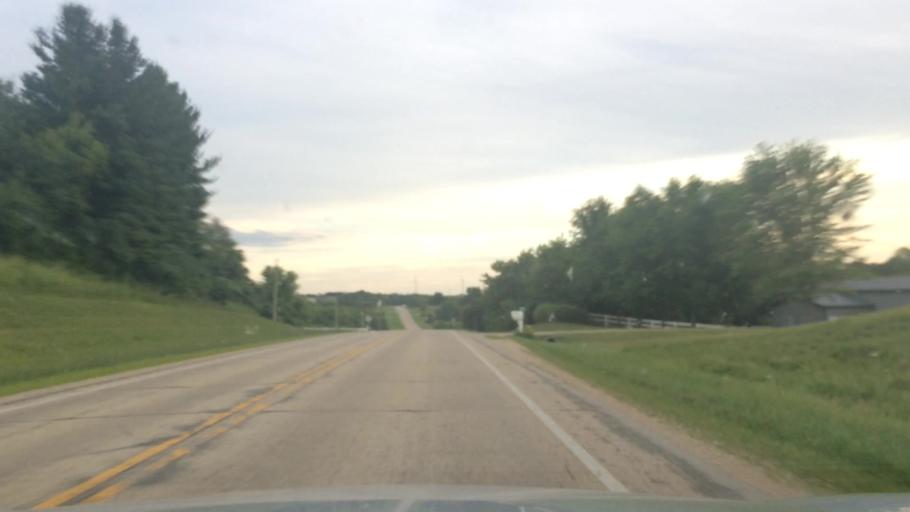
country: US
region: Wisconsin
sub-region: Dane County
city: Waunakee
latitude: 43.2093
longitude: -89.5476
